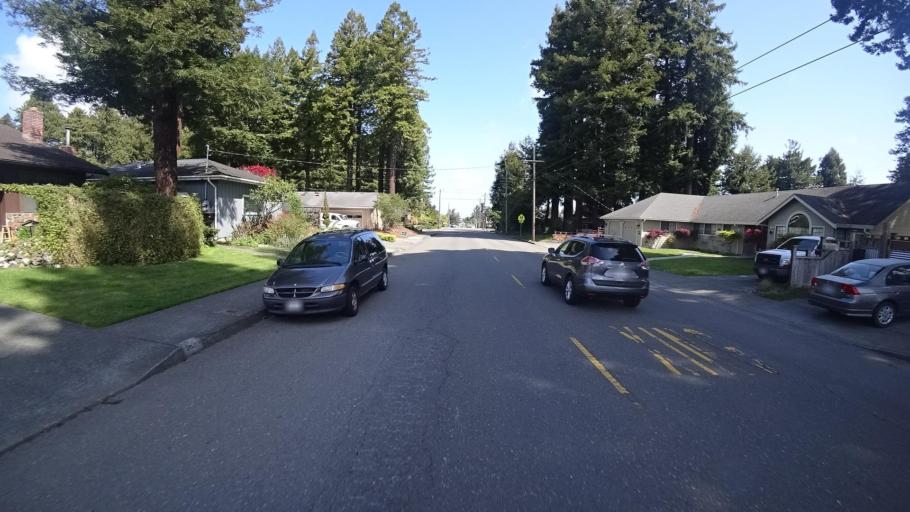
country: US
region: California
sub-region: Humboldt County
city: Cutten
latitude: 40.7782
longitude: -124.1397
